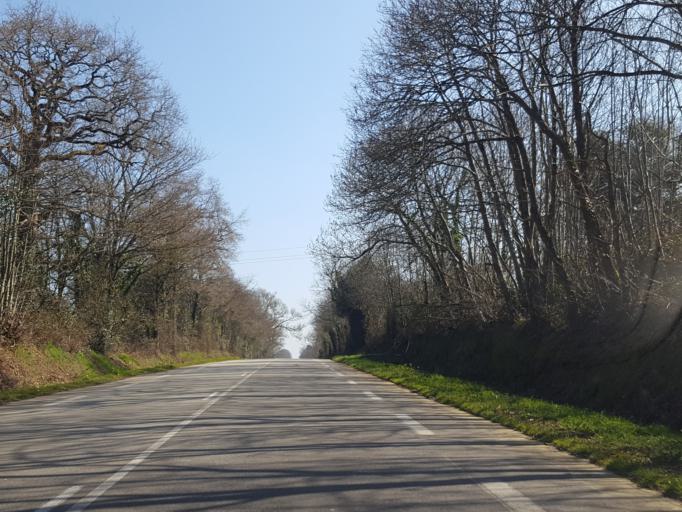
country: FR
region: Pays de la Loire
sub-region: Departement de la Vendee
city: La Roche-sur-Yon
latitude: 46.6618
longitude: -1.3918
